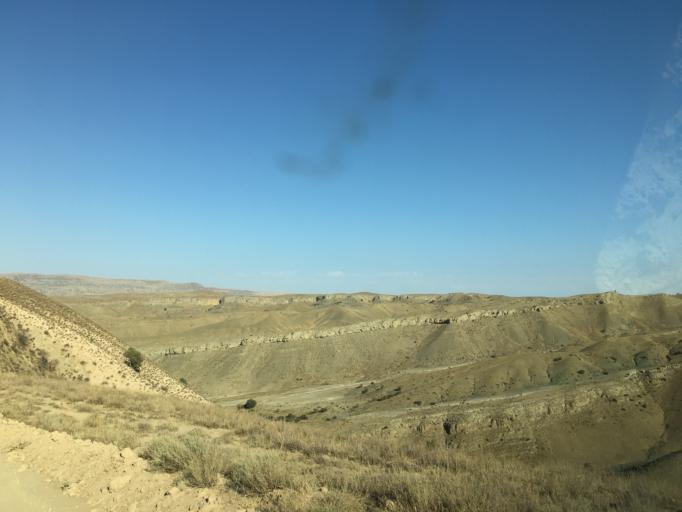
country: TM
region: Balkan
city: Magtymguly
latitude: 38.3011
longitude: 56.7926
